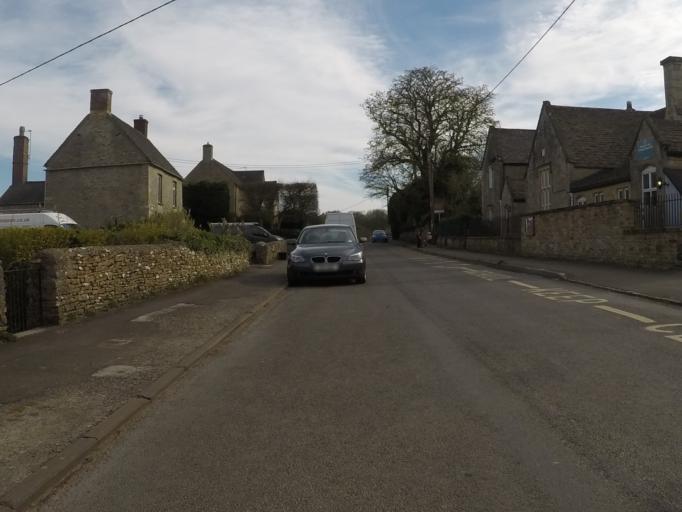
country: GB
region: England
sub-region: Oxfordshire
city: Charlbury
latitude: 51.8452
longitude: -1.4768
